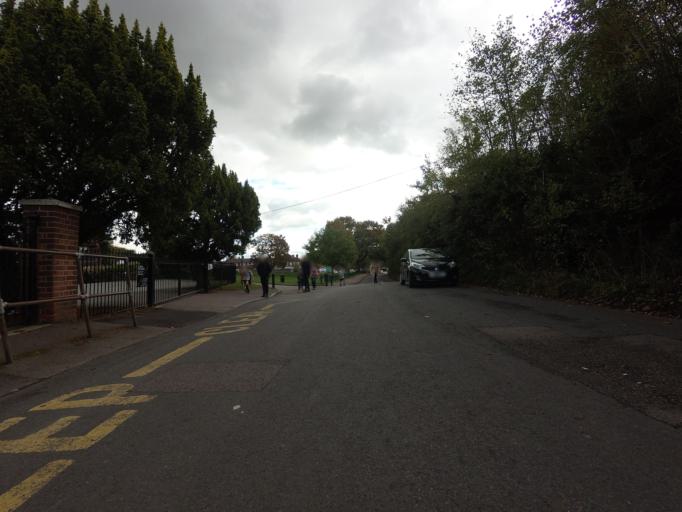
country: GB
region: England
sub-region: Kent
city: Swanley
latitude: 51.3852
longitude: 0.1605
